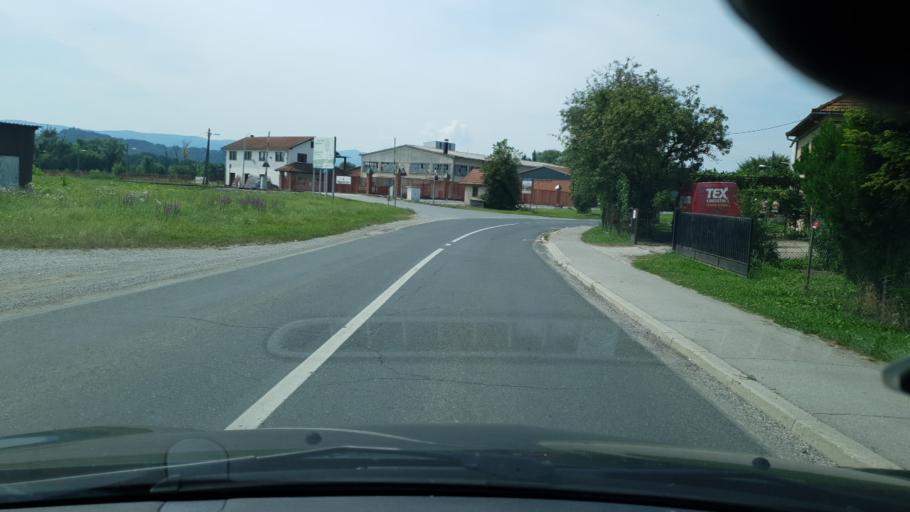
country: HR
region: Krapinsko-Zagorska
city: Bedekovcina
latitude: 46.0435
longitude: 16.0021
